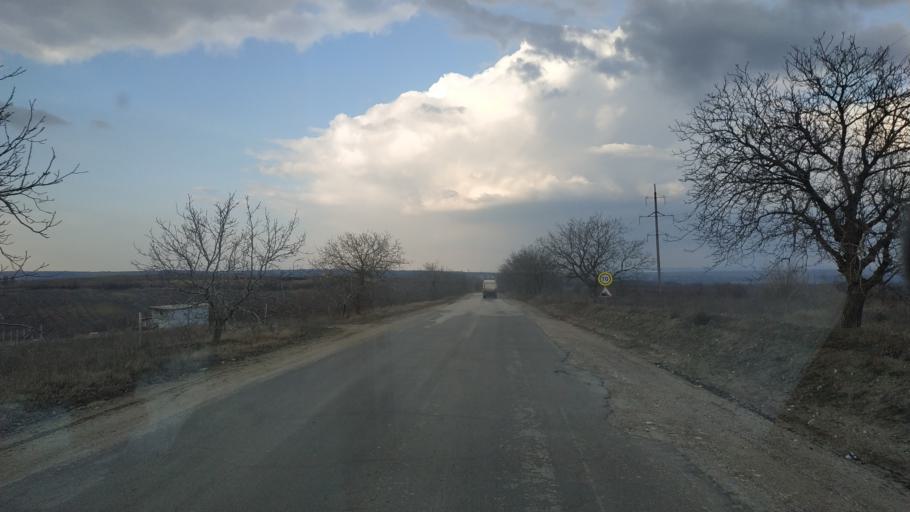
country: MD
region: Anenii Noi
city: Anenii Noi
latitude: 46.9642
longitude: 29.2846
